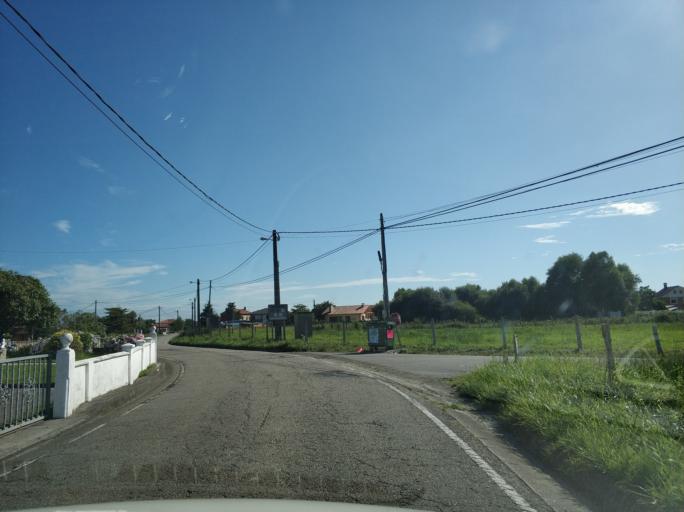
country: ES
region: Asturias
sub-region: Province of Asturias
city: Cudillero
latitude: 43.5687
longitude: -6.2378
